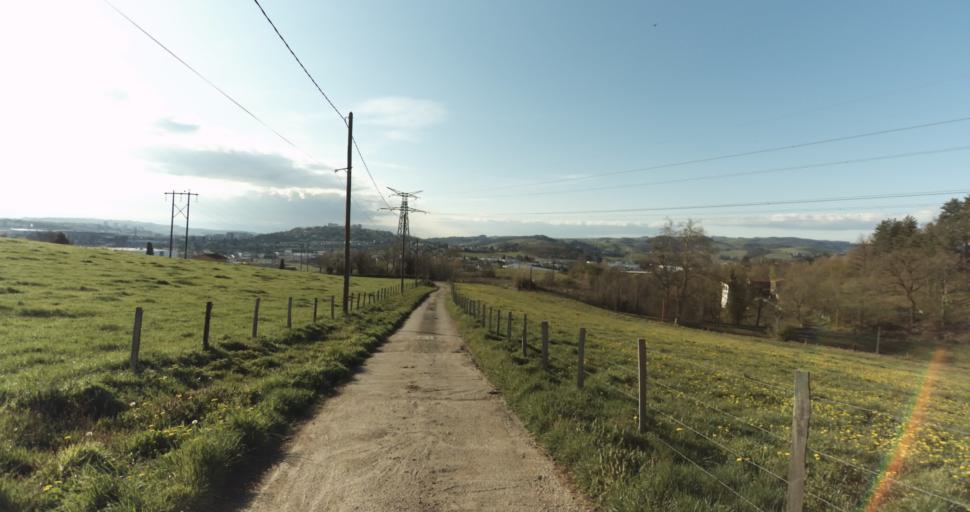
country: FR
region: Rhone-Alpes
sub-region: Departement de la Loire
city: Saint-Jean-Bonnefonds
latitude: 45.4578
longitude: 4.4292
